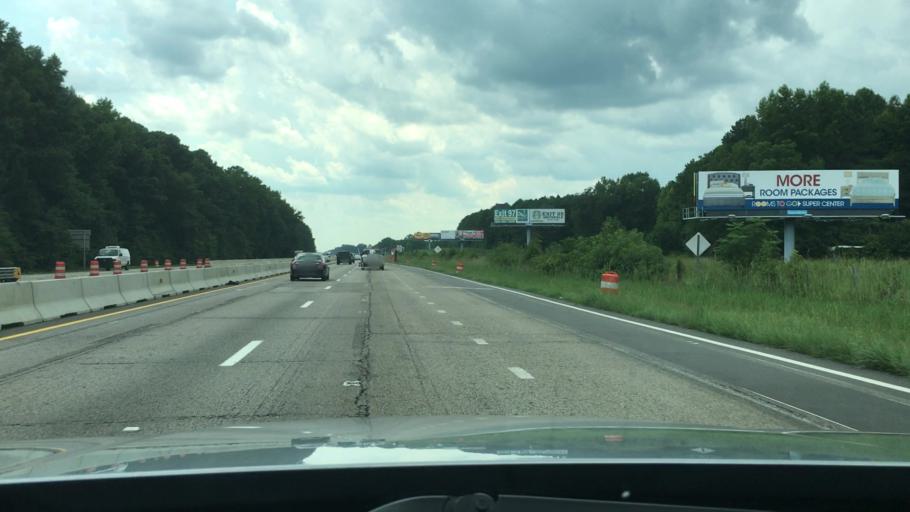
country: US
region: North Carolina
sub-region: Johnston County
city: Pine Level
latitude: 35.5555
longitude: -78.2043
